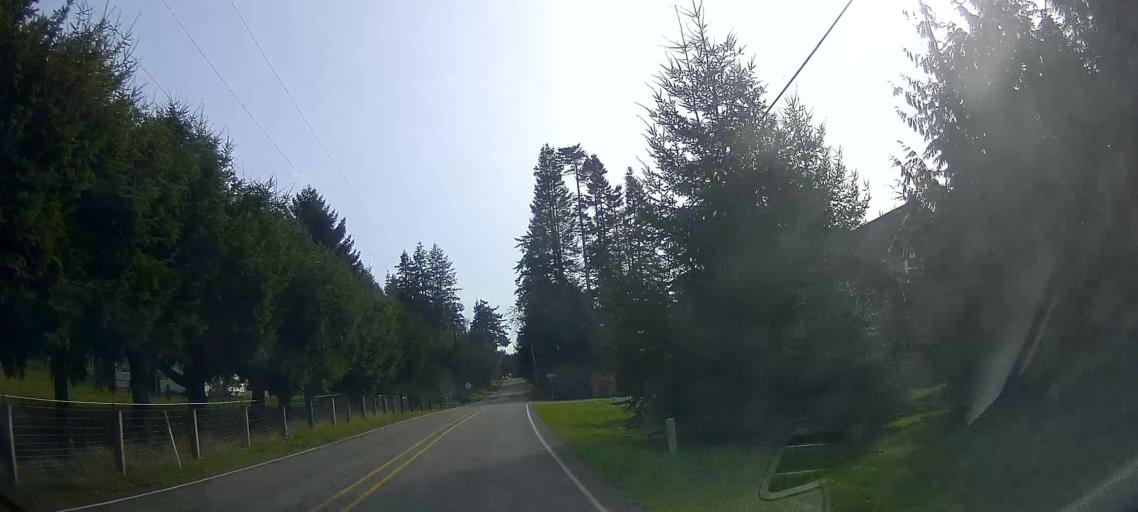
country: US
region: Washington
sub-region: Island County
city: Langley
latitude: 48.0865
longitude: -122.3982
